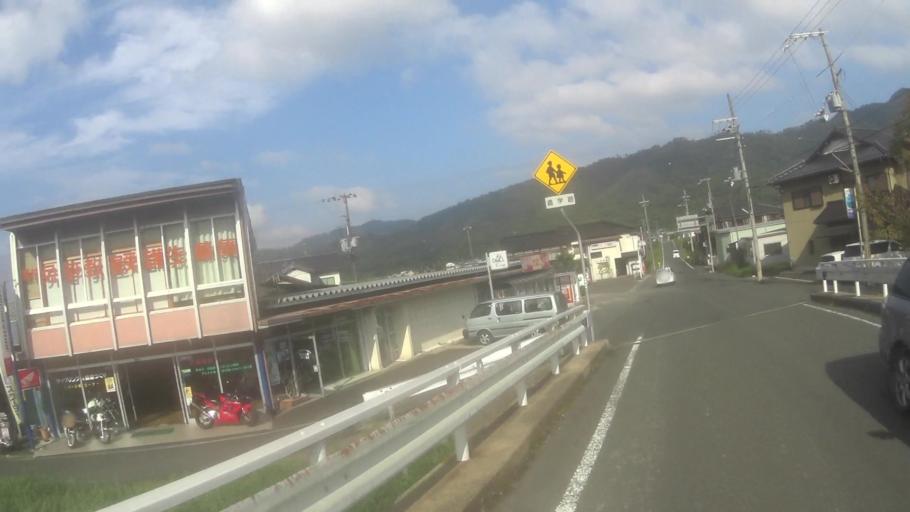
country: JP
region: Kyoto
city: Miyazu
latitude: 35.5373
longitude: 135.1258
